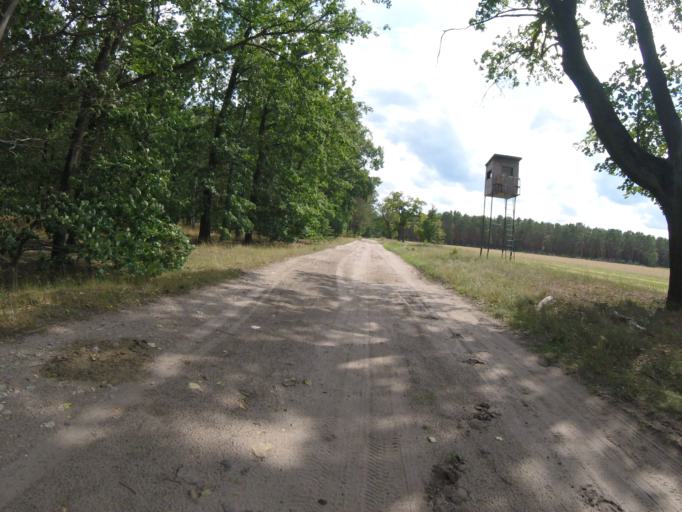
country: DE
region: Brandenburg
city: Halbe
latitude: 52.1416
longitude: 13.6953
